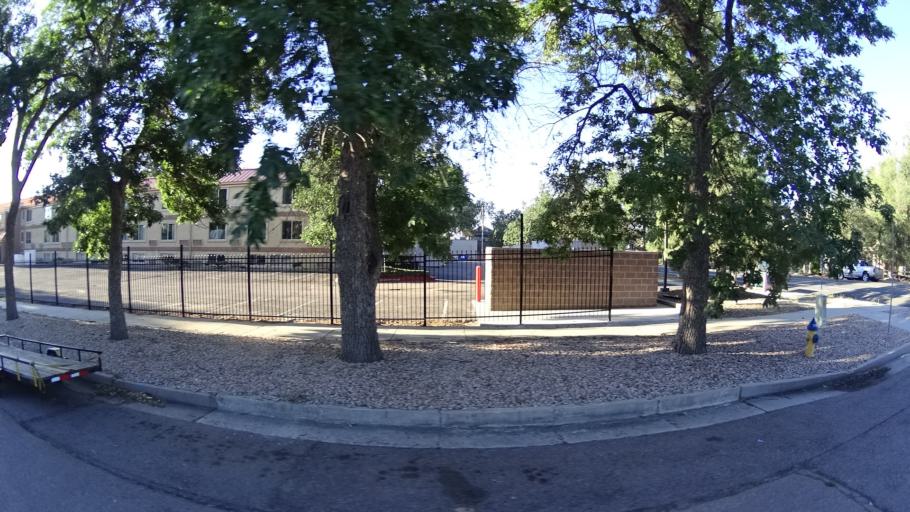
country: US
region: Colorado
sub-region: El Paso County
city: Colorado Springs
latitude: 38.8384
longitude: -104.8323
